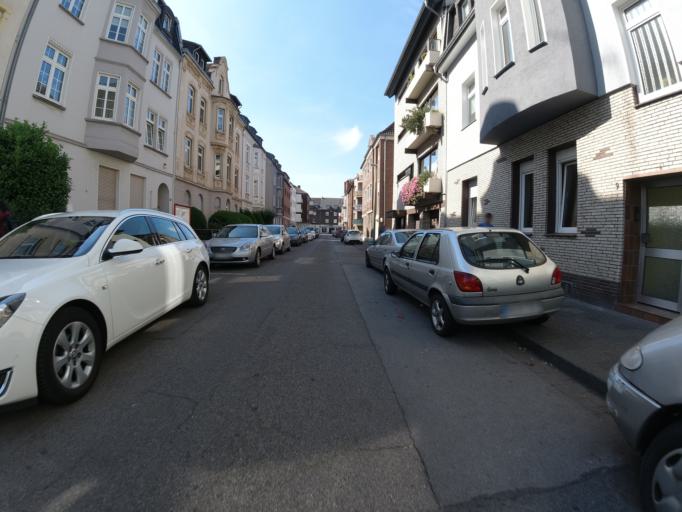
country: DE
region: North Rhine-Westphalia
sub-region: Regierungsbezirk Dusseldorf
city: Hochfeld
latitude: 51.4079
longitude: 6.7164
